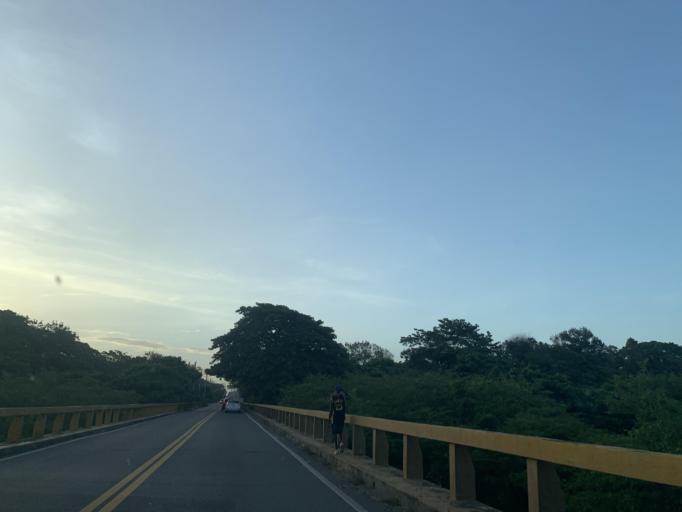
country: DO
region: Puerto Plata
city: Imbert
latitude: 19.7362
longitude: -70.8354
